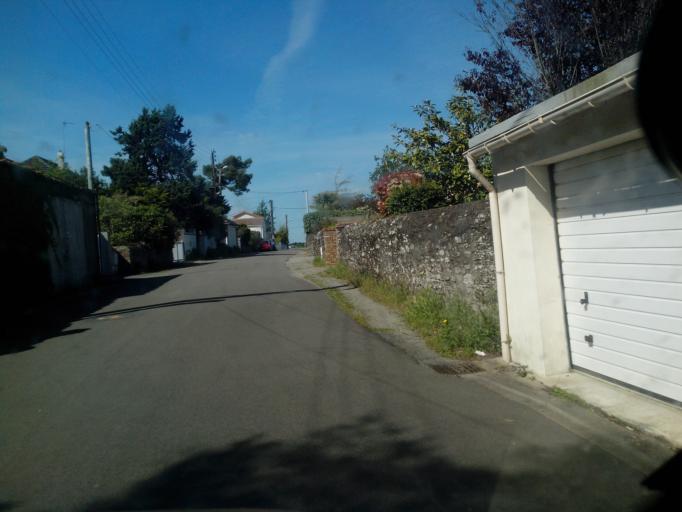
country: FR
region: Pays de la Loire
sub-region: Departement de la Loire-Atlantique
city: Pornic
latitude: 47.1078
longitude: -2.0887
